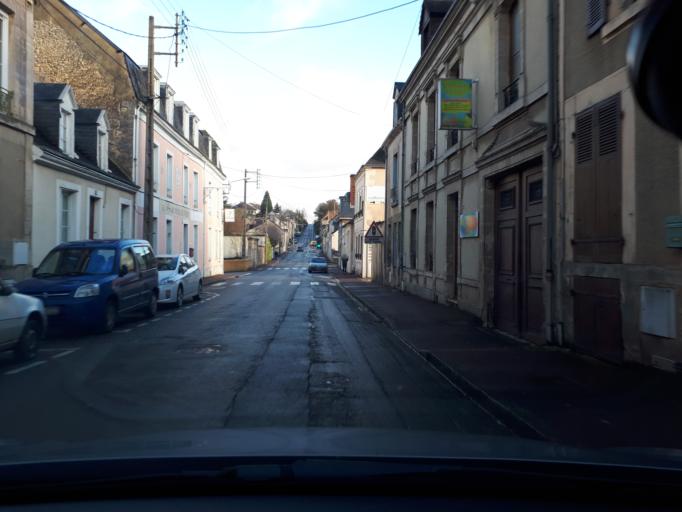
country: FR
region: Pays de la Loire
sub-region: Departement de la Sarthe
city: Mamers
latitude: 48.3506
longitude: 0.3726
